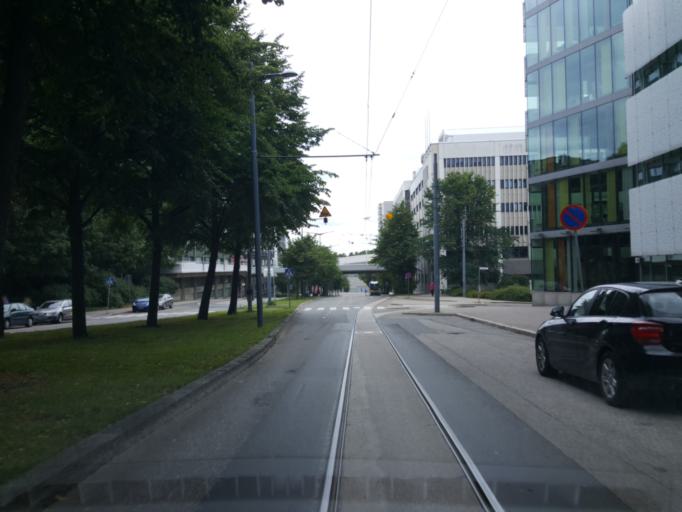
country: FI
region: Uusimaa
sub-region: Helsinki
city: Helsinki
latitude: 60.1994
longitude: 24.9400
